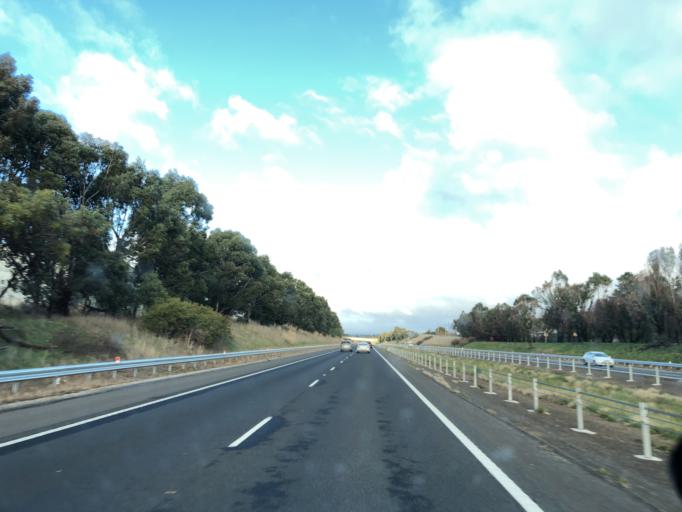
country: AU
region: Victoria
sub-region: Mount Alexander
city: Castlemaine
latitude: -37.2339
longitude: 144.4500
